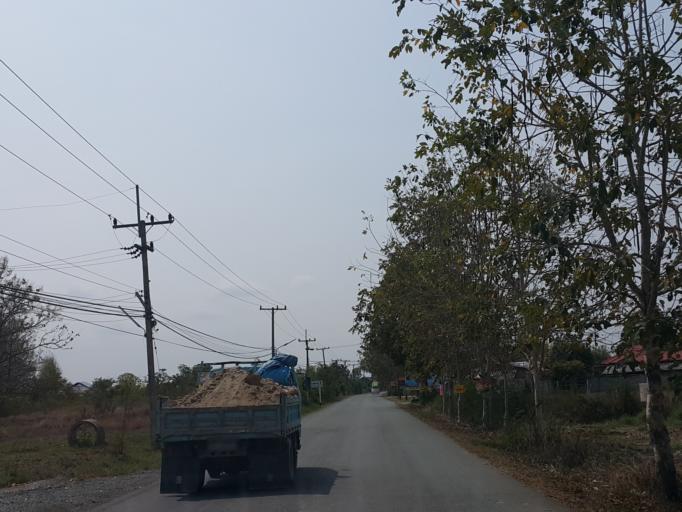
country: TH
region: Lamphun
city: Ban Thi
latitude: 18.6827
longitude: 99.1016
